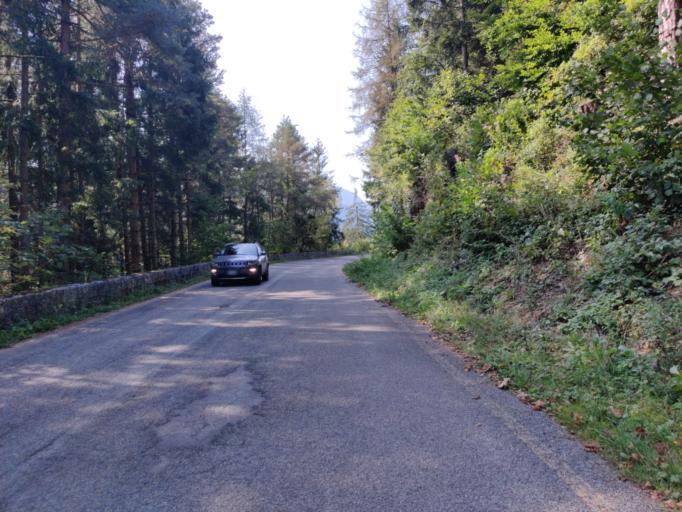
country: IT
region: Friuli Venezia Giulia
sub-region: Provincia di Udine
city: Tarvisio
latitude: 46.5139
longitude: 13.6124
